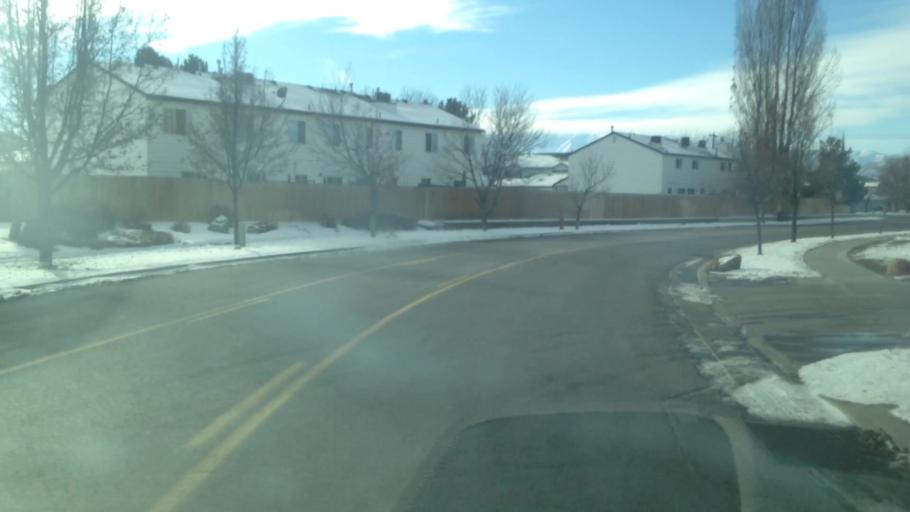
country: US
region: Utah
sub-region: Cache County
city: Logan
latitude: 41.7542
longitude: -111.8378
